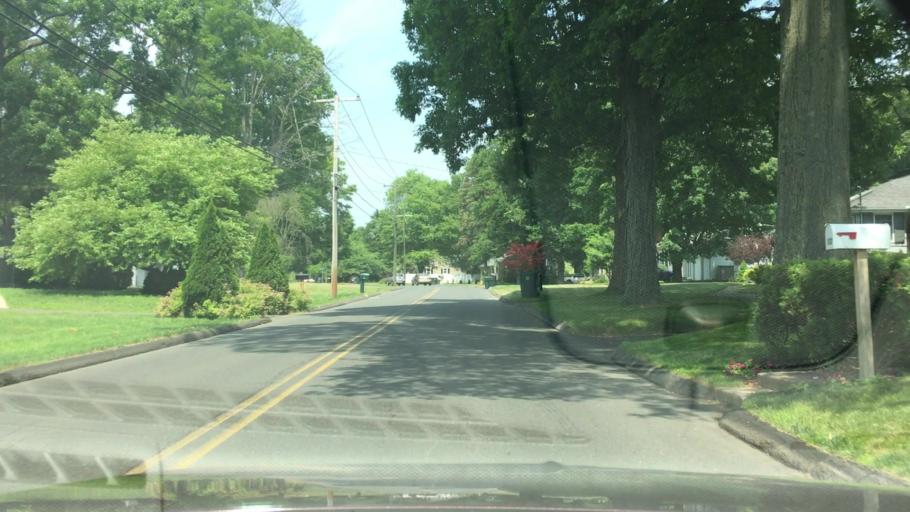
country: US
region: Connecticut
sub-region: New Haven County
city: Cheshire Village
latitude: 41.5144
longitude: -72.9189
